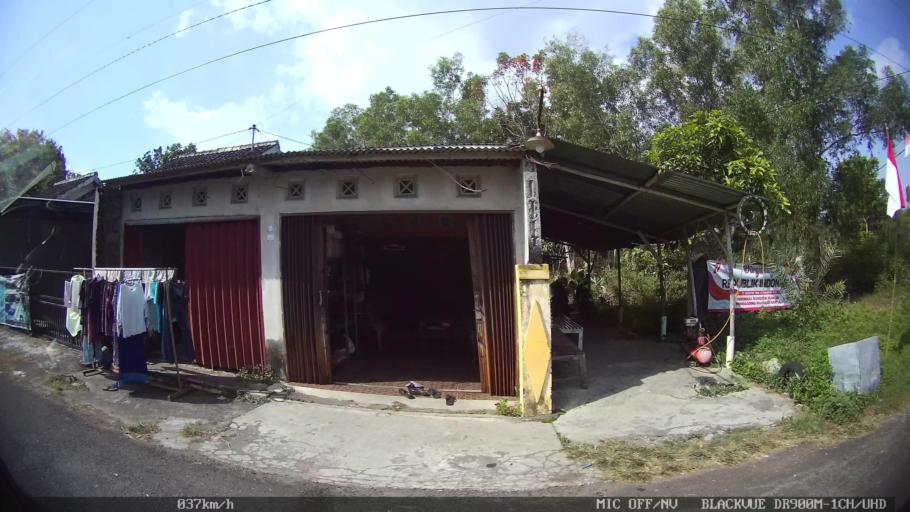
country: ID
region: Daerah Istimewa Yogyakarta
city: Bantul
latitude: -7.8603
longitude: 110.3054
